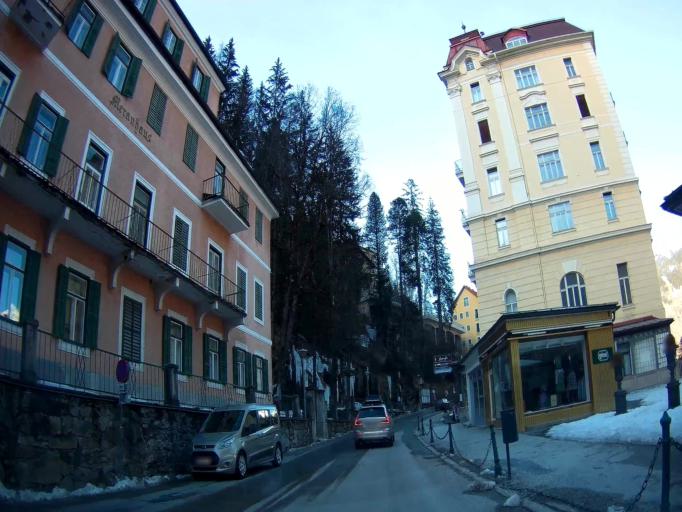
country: AT
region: Salzburg
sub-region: Politischer Bezirk Sankt Johann im Pongau
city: Bad Gastein
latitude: 47.1143
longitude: 13.1342
